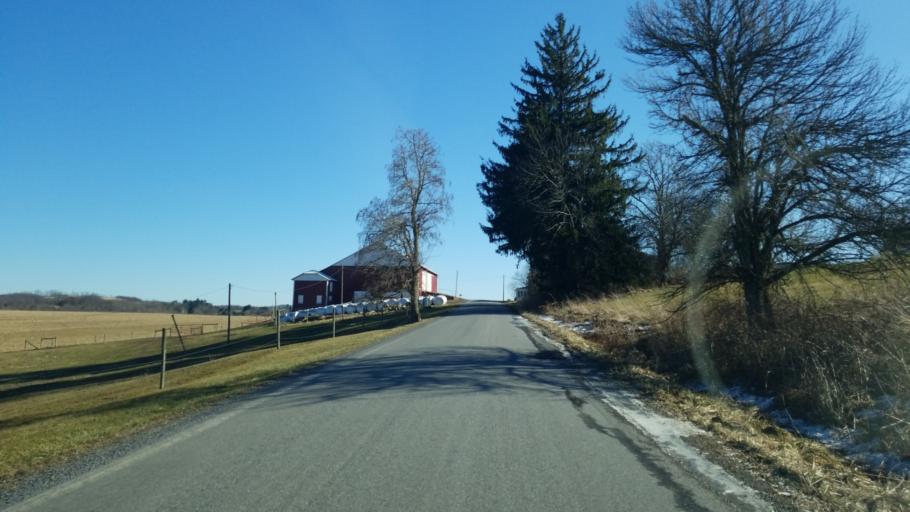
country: US
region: Pennsylvania
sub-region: Jefferson County
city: Sykesville
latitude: 41.0433
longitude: -78.7846
